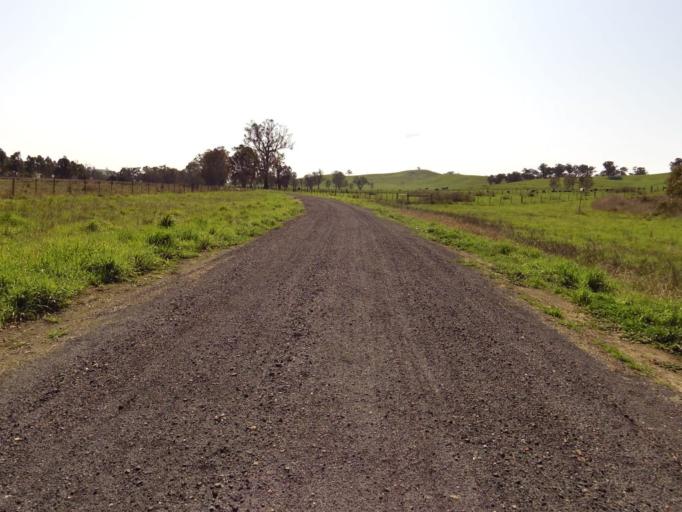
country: AU
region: Victoria
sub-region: Murrindindi
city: Alexandra
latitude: -37.1483
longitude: 145.5871
